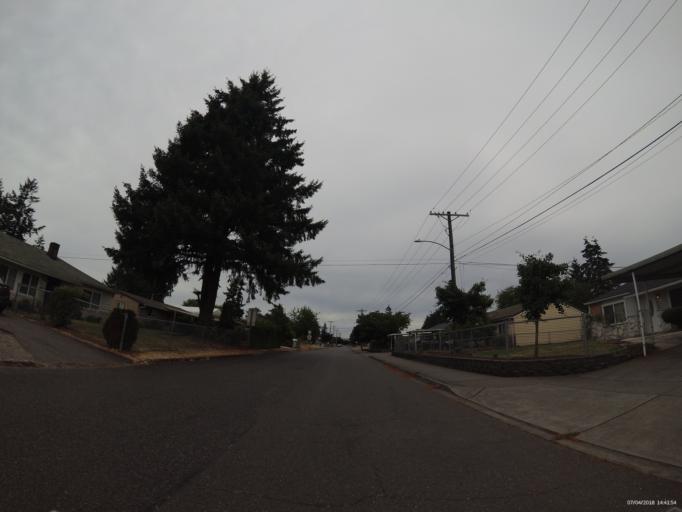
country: US
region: Washington
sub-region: Pierce County
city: Lakewood
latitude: 47.1628
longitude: -122.4995
